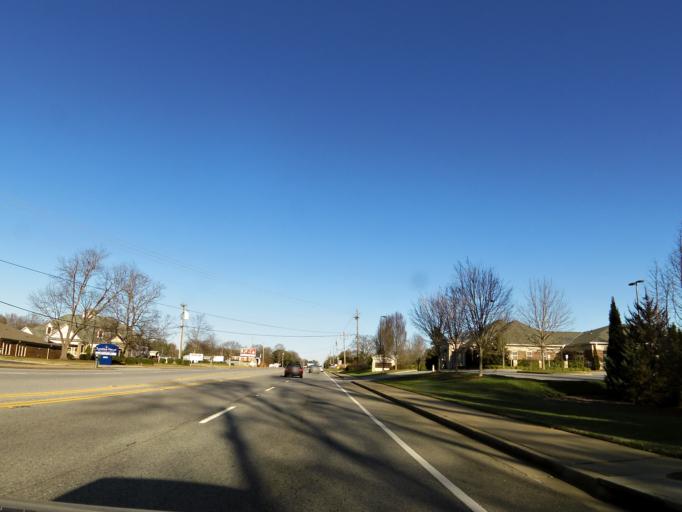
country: US
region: South Carolina
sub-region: Spartanburg County
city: Fairforest
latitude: 34.9126
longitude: -82.0134
